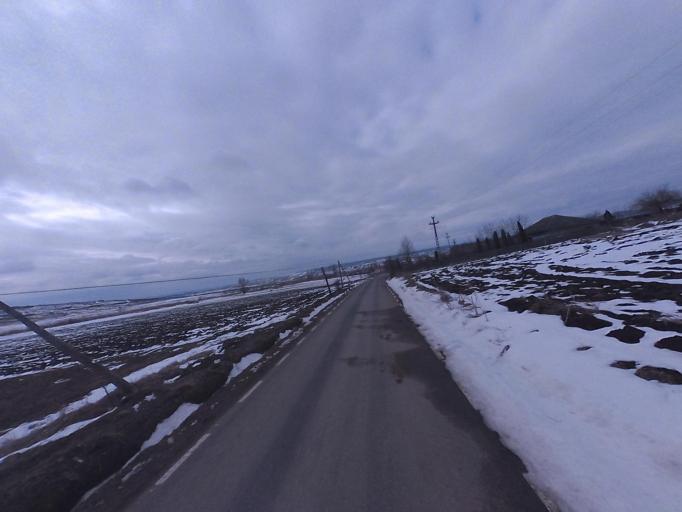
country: RO
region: Iasi
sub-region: Comuna Tibana
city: Tibana
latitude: 46.9808
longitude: 27.3479
